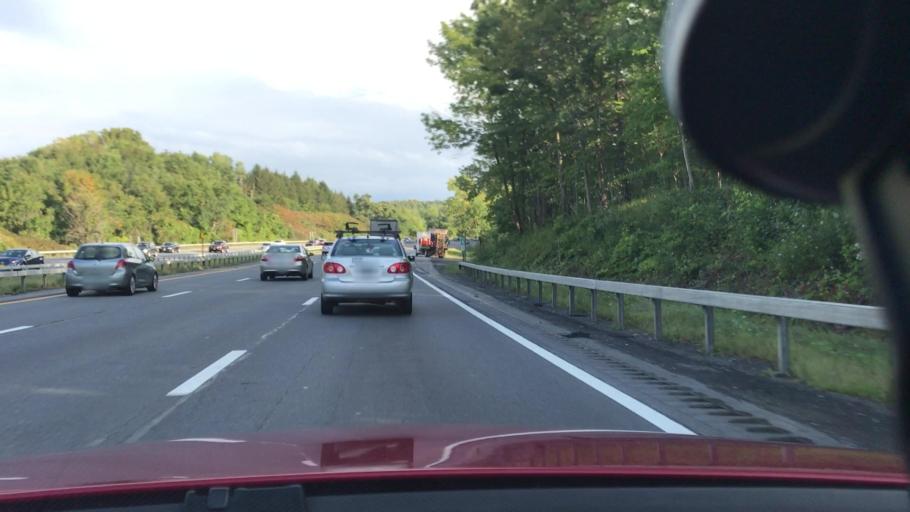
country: US
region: New York
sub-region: Albany County
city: Cohoes
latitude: 42.7904
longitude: -73.7603
